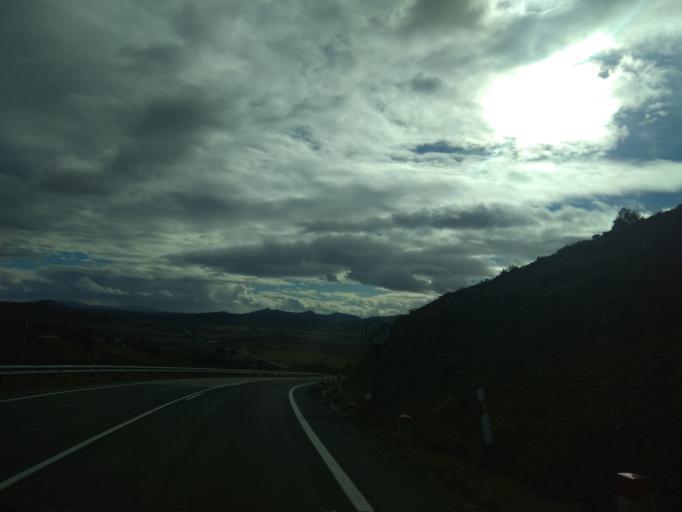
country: ES
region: Castille and Leon
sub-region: Provincia de Burgos
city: Arija
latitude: 43.0344
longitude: -3.8667
